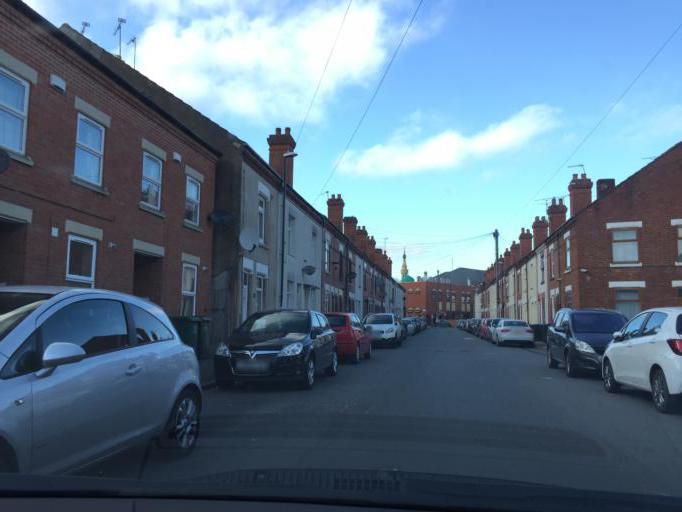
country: GB
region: England
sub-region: Coventry
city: Coventry
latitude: 52.4178
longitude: -1.4982
